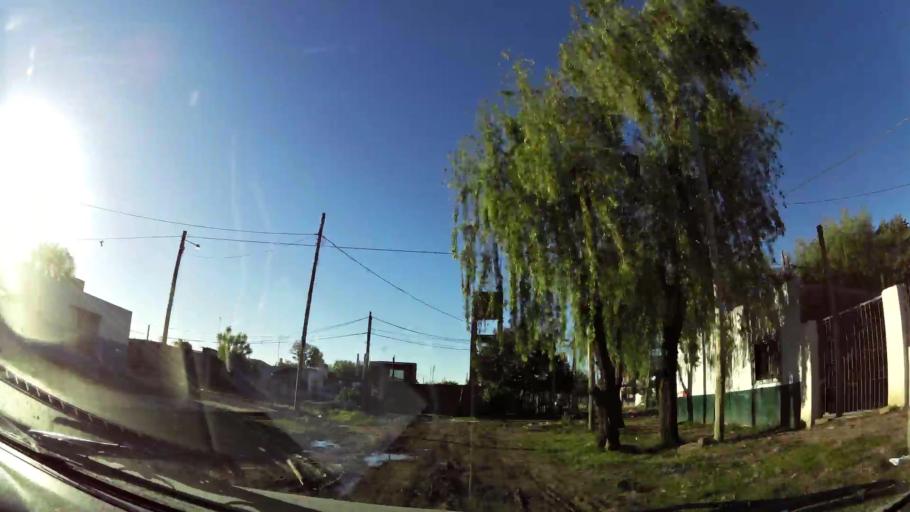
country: AR
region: Buenos Aires
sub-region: Partido de Almirante Brown
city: Adrogue
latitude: -34.7741
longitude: -58.3411
